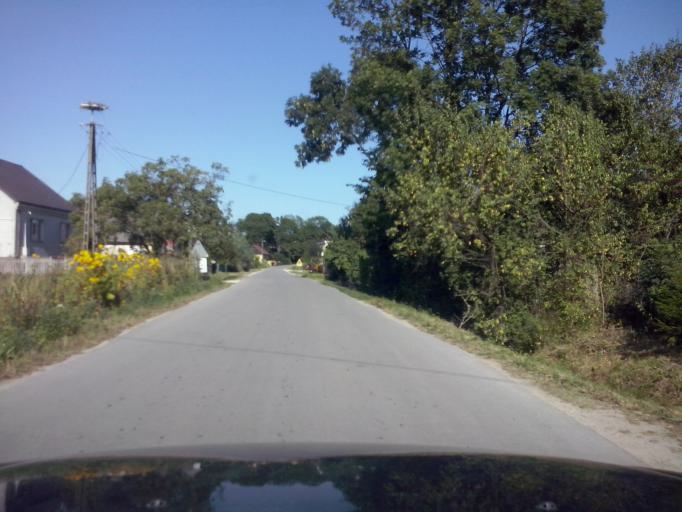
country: PL
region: Swietokrzyskie
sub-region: Powiat pinczowski
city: Kije
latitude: 50.5799
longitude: 20.6496
